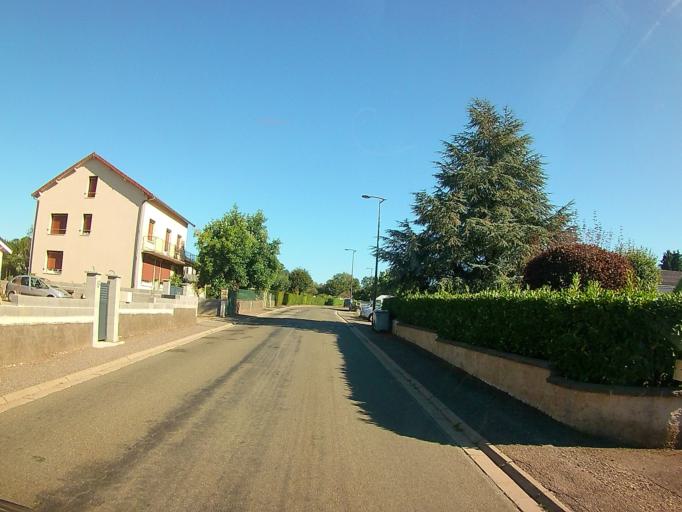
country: FR
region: Auvergne
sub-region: Departement du Puy-de-Dome
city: Chapdes-Beaufort
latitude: 45.8905
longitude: 2.8669
